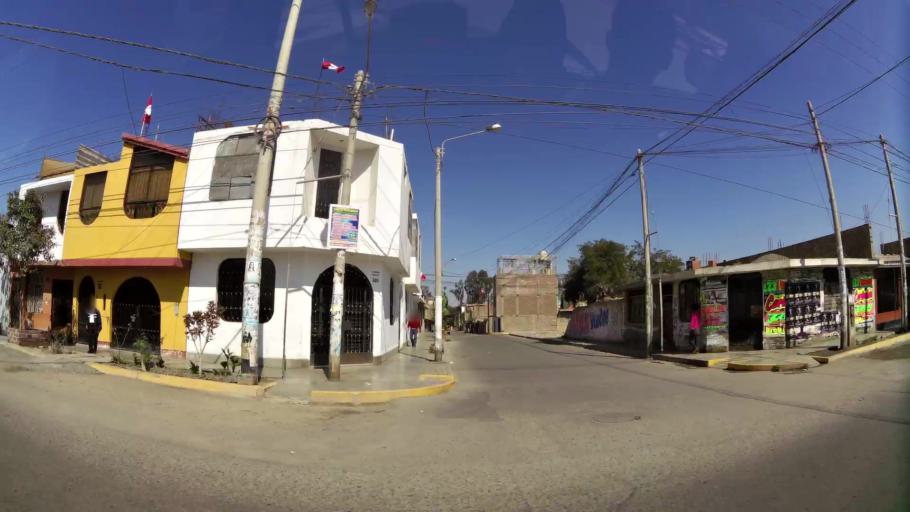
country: PE
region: Ica
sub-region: Provincia de Ica
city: La Tinguina
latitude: -14.0408
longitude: -75.7104
